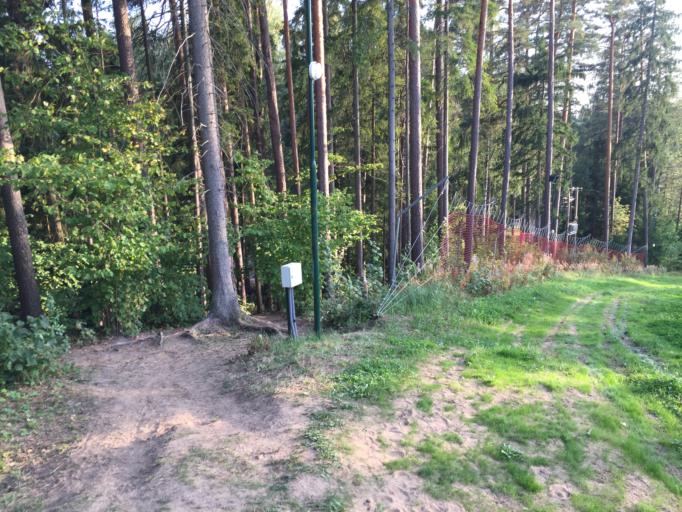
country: LV
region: Baldone
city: Baldone
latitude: 56.7746
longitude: 24.4018
